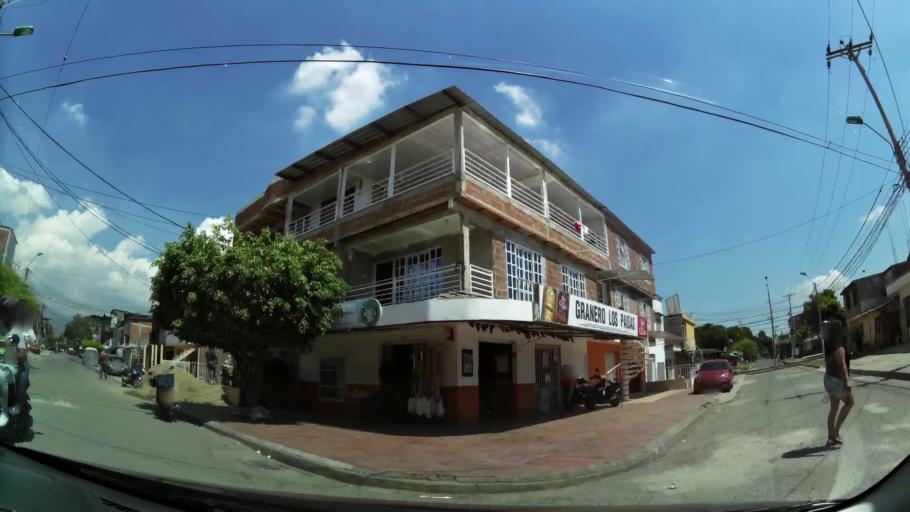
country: CO
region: Valle del Cauca
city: Cali
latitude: 3.4313
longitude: -76.4994
